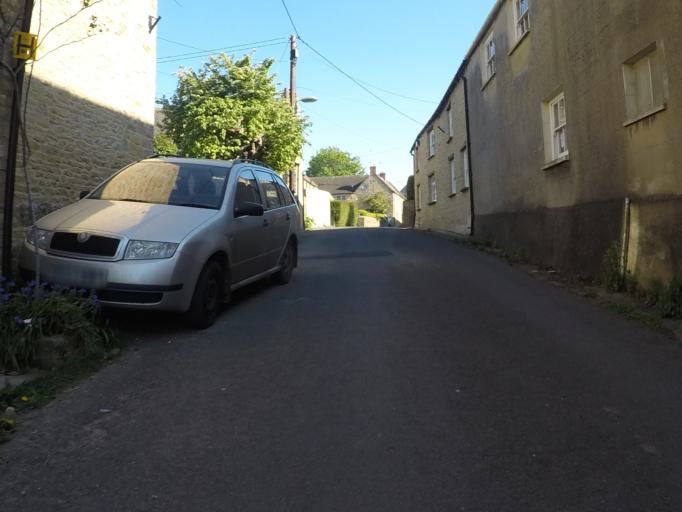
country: GB
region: England
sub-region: Oxfordshire
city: Charlbury
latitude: 51.8704
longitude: -1.4800
